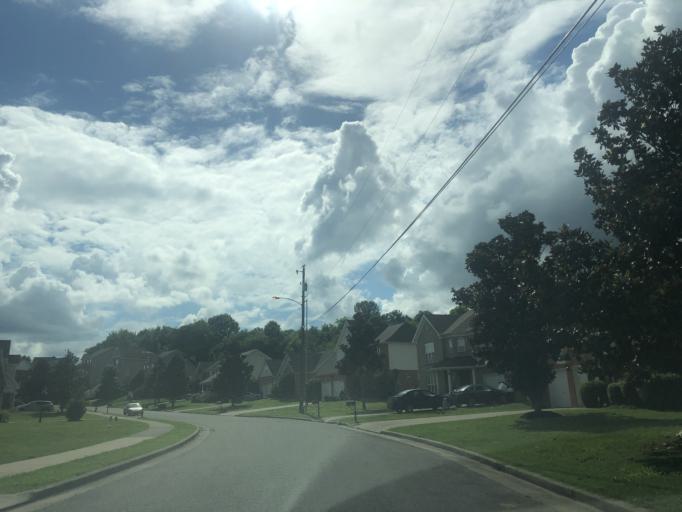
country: US
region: Tennessee
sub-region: Davidson County
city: Nashville
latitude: 36.2231
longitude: -86.8670
